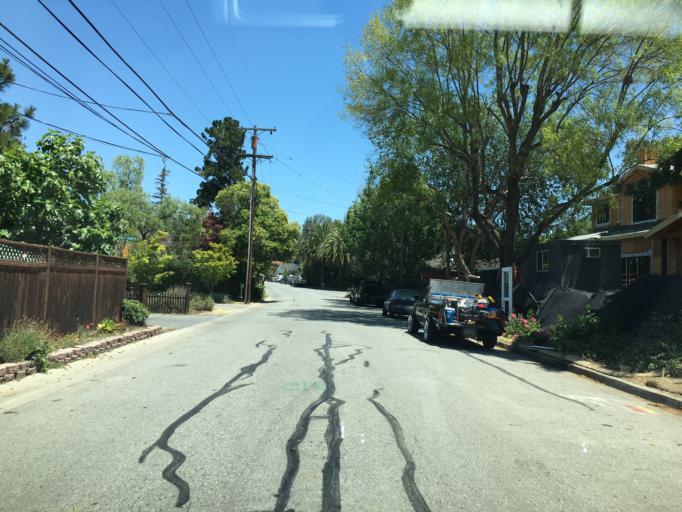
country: US
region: California
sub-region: San Mateo County
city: West Menlo Park
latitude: 37.4387
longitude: -122.2073
